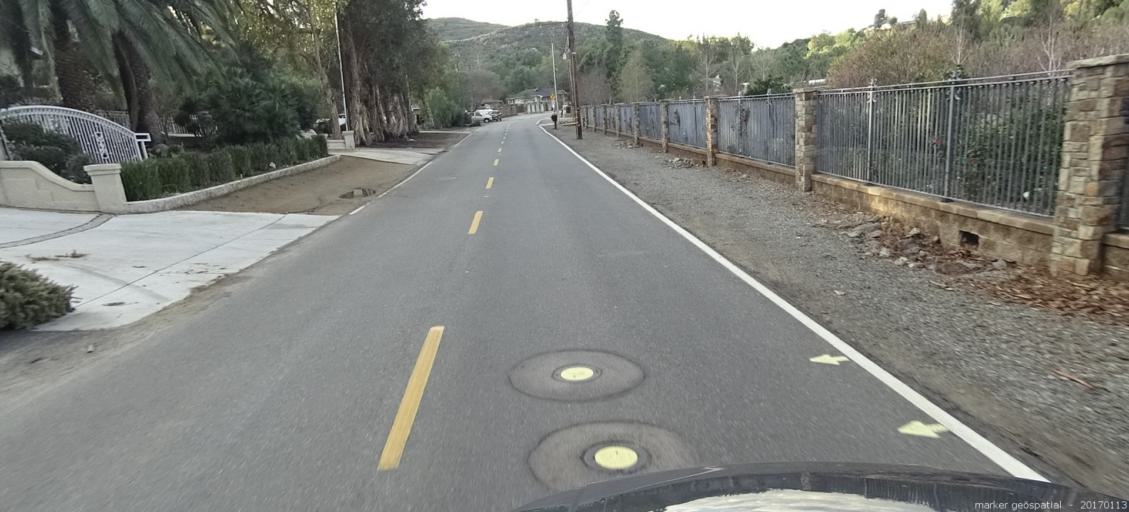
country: US
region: California
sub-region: Orange County
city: Villa Park
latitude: 33.8010
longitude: -117.7856
